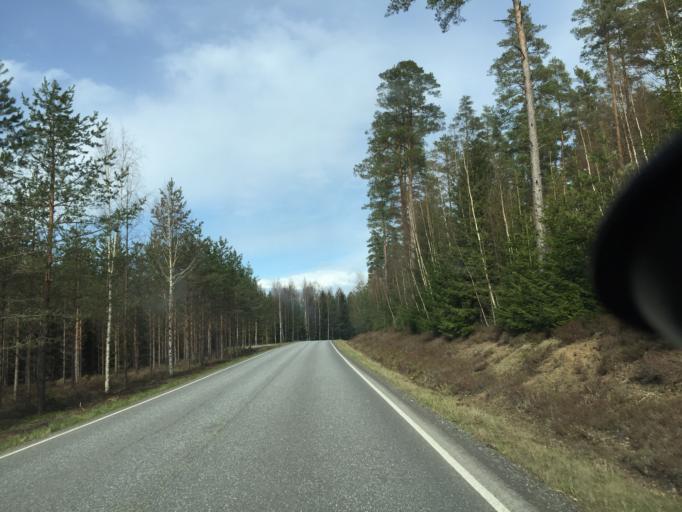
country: FI
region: Varsinais-Suomi
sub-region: Salo
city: Pernioe
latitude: 60.0245
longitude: 23.1783
